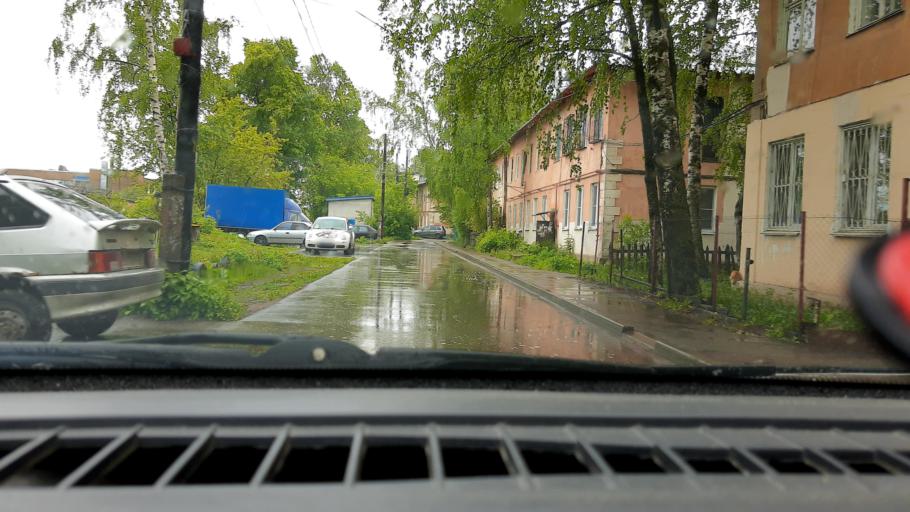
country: RU
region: Nizjnij Novgorod
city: Nizhniy Novgorod
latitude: 56.3040
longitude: 43.8852
